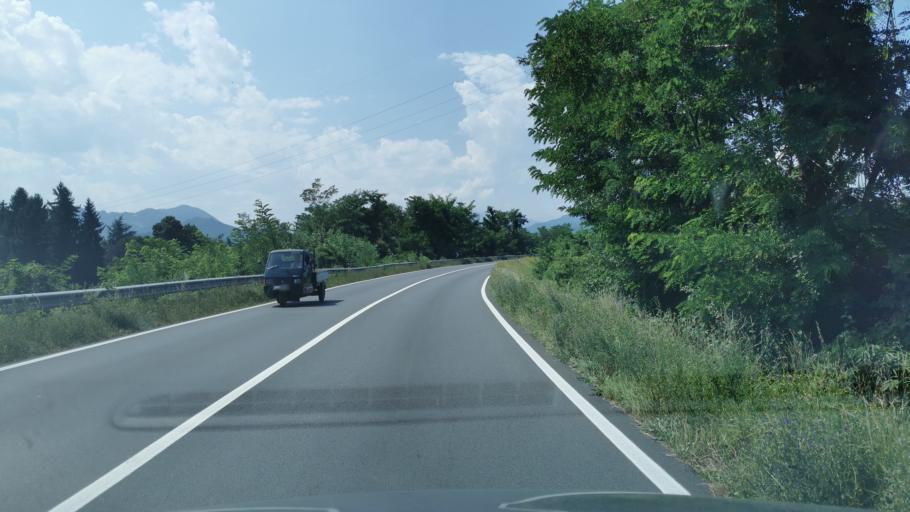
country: IT
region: Piedmont
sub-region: Provincia di Cuneo
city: Borgo San Dalmazzo
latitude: 44.3309
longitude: 7.5130
